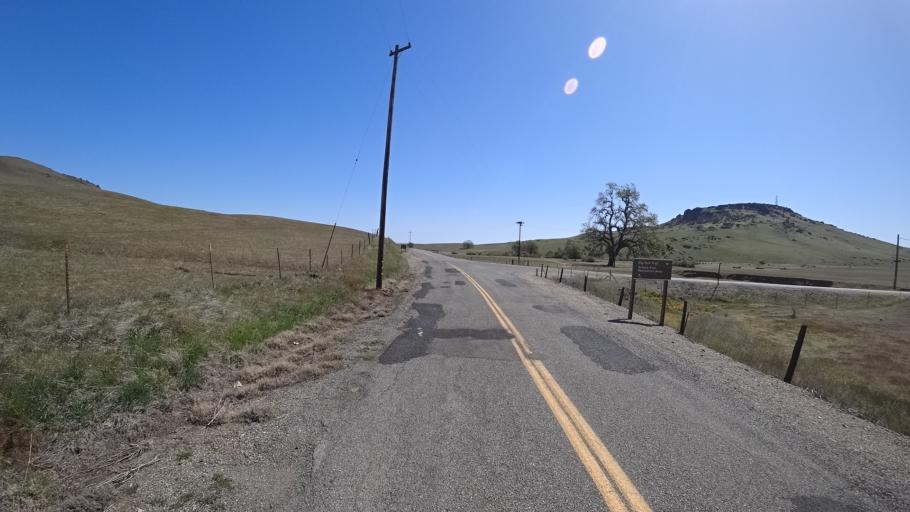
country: US
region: California
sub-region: Glenn County
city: Orland
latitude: 39.7629
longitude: -122.3410
